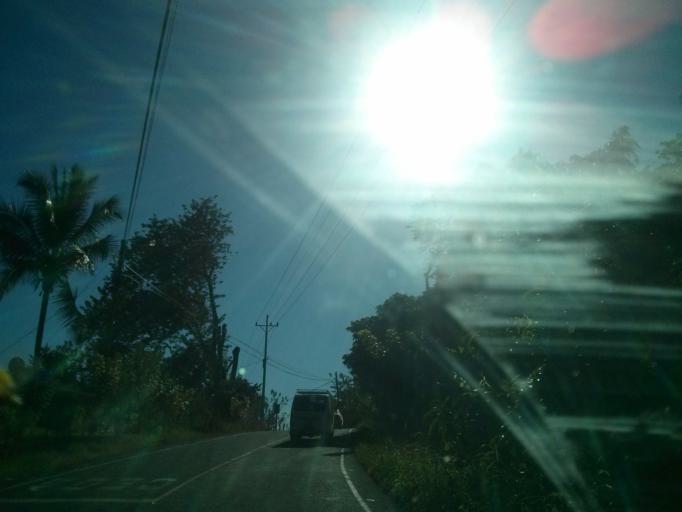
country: CR
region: Puntarenas
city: Paquera
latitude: 9.6999
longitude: -85.0608
